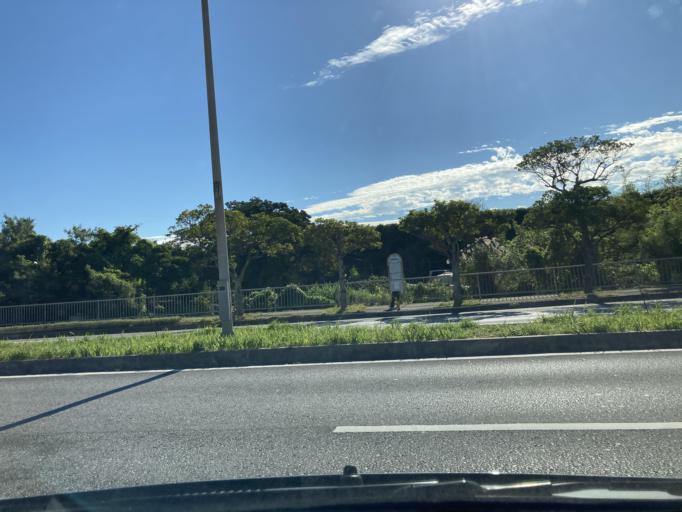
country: JP
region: Okinawa
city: Okinawa
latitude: 26.3672
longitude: 127.7737
